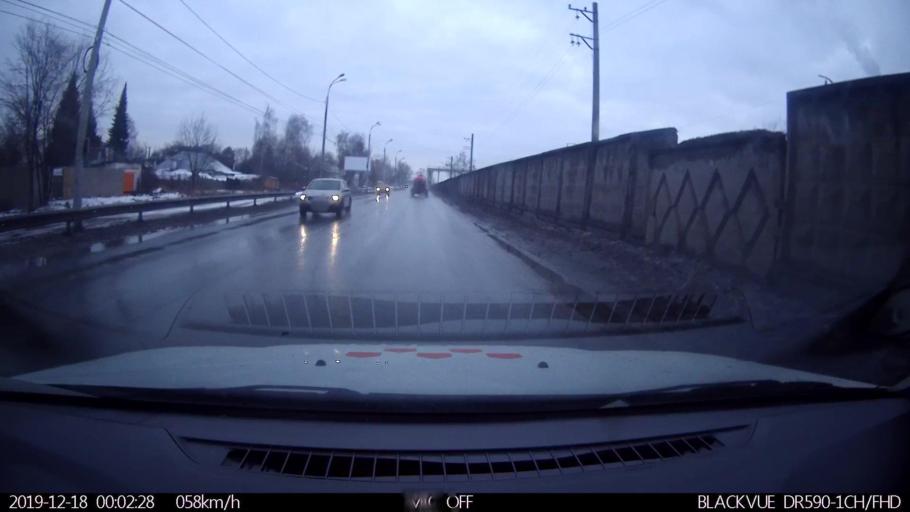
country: RU
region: Nizjnij Novgorod
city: Gorbatovka
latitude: 56.3680
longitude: 43.8283
